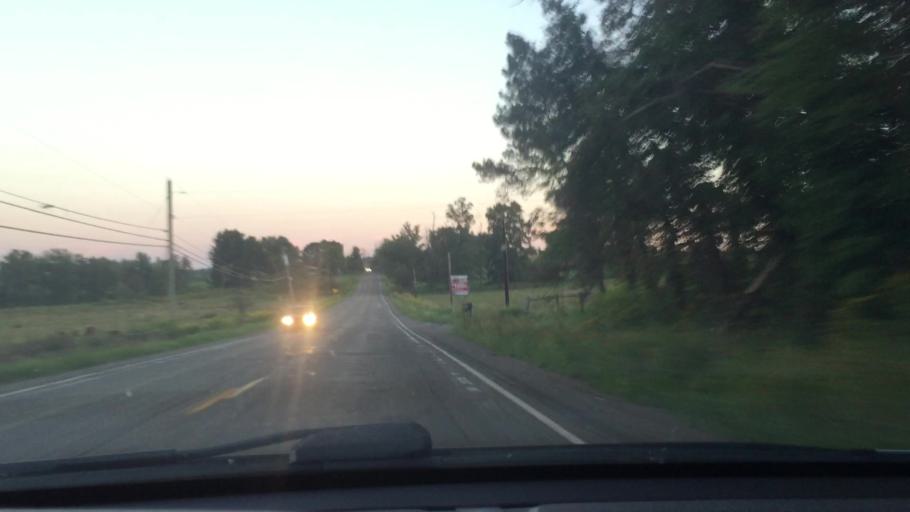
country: US
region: Pennsylvania
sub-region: Butler County
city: Slippery Rock
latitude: 41.1053
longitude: -80.0533
